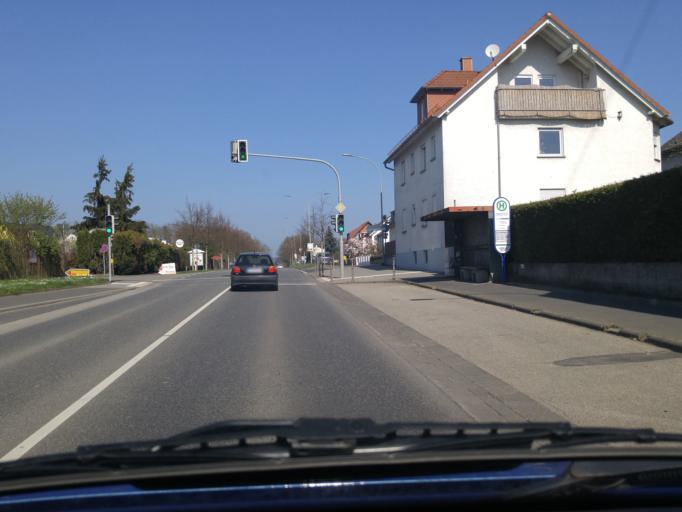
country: DE
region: Hesse
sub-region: Regierungsbezirk Darmstadt
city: Karben
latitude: 50.2832
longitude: 8.7699
